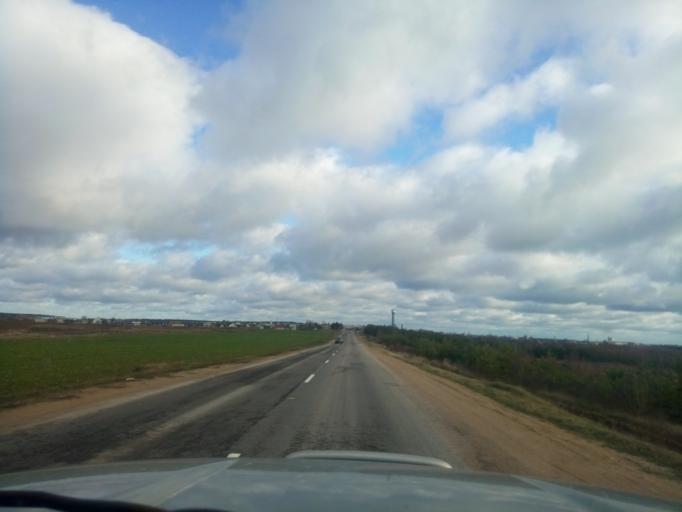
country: BY
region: Minsk
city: Kapyl'
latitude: 53.1487
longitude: 27.0625
